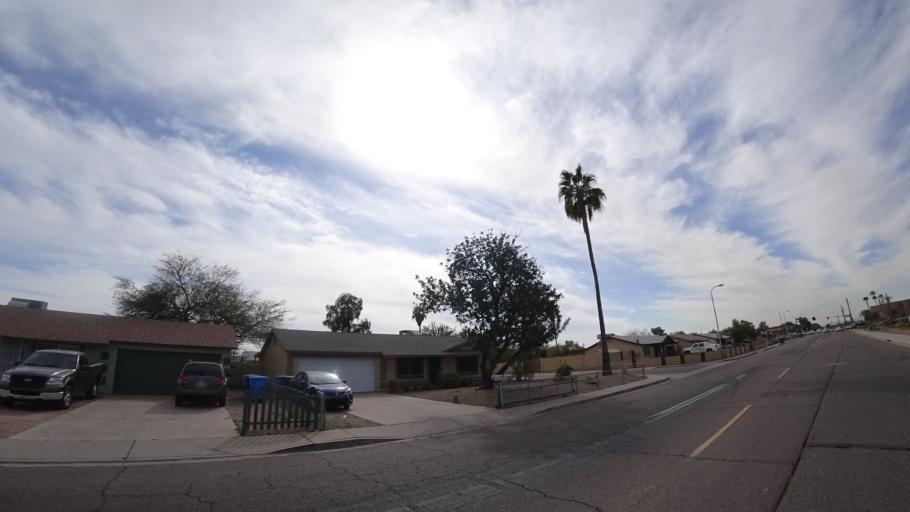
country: US
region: Arizona
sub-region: Maricopa County
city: Tolleson
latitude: 33.4730
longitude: -112.2185
